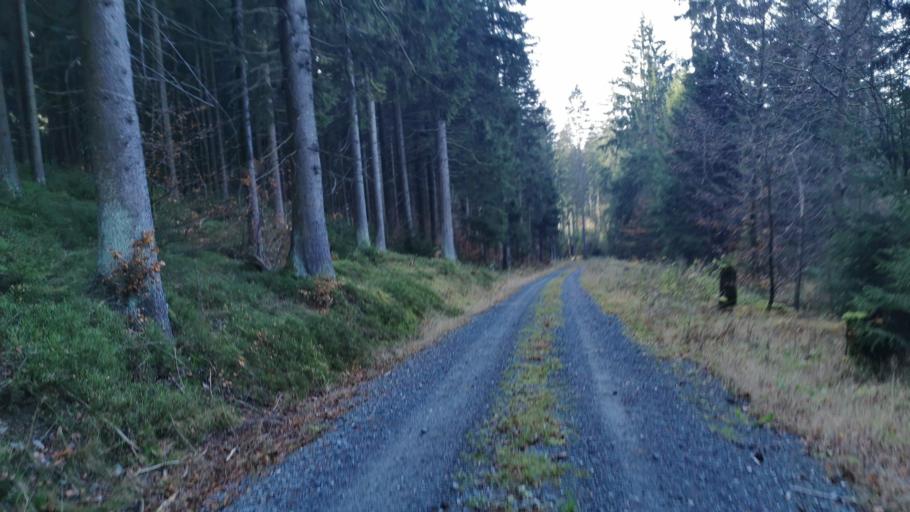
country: DE
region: Bavaria
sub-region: Upper Franconia
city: Tschirn
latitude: 50.4426
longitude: 11.4622
